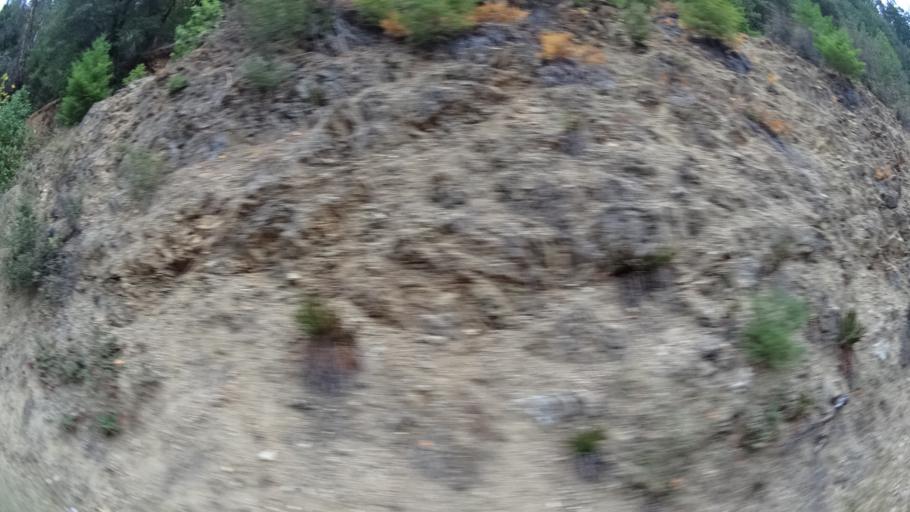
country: US
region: California
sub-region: Siskiyou County
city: Happy Camp
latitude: 41.8936
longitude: -123.4335
